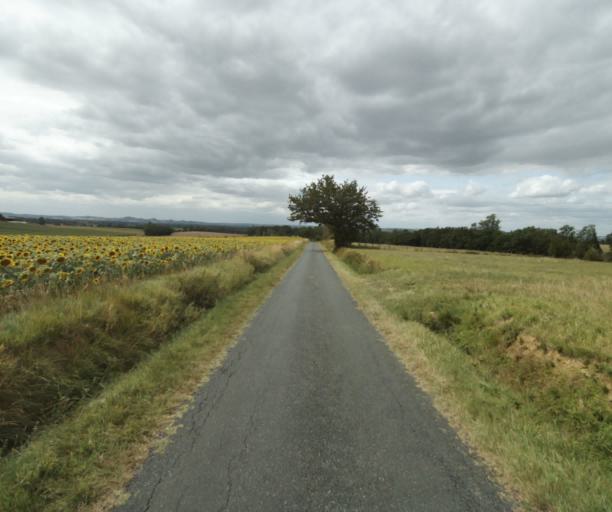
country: FR
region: Midi-Pyrenees
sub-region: Departement du Tarn
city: Soreze
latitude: 43.4629
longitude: 2.0715
